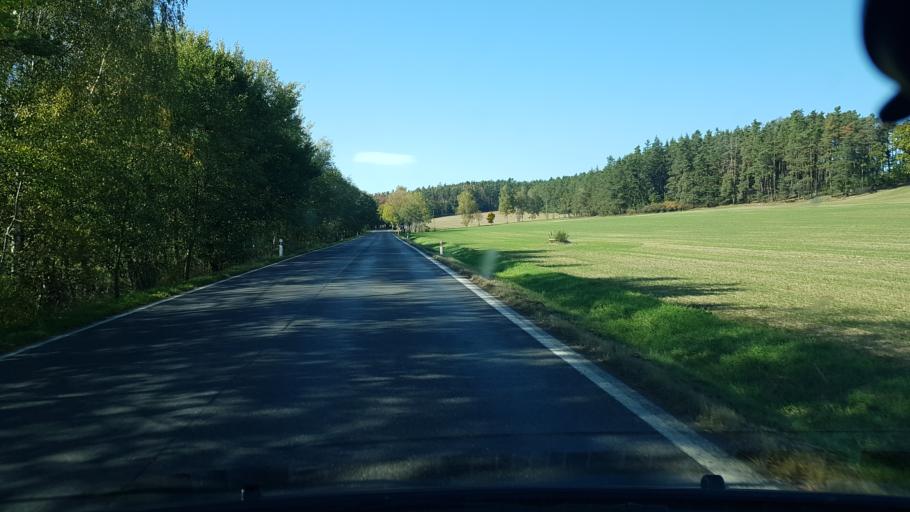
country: CZ
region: Jihocesky
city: Radomysl
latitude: 49.2965
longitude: 14.0211
